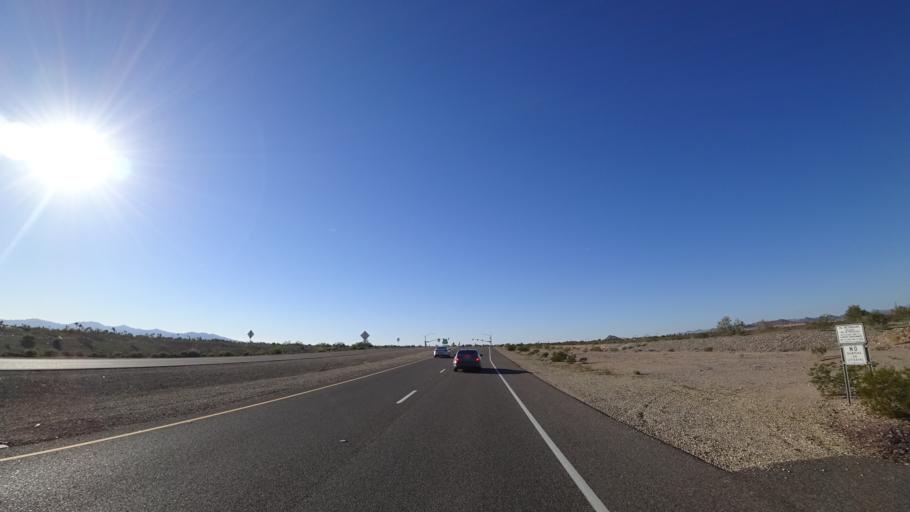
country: US
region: Arizona
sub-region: Maricopa County
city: Sun City West
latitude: 33.6837
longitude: -112.3262
